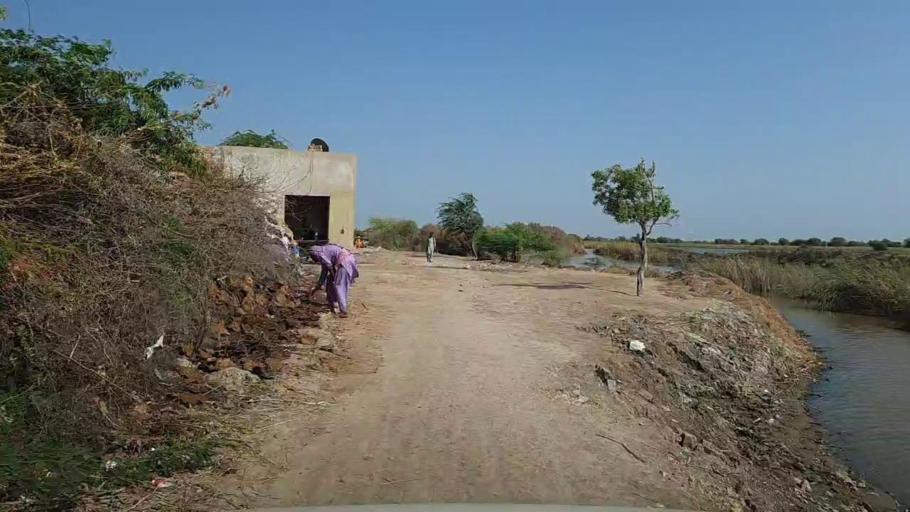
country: PK
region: Sindh
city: Kario
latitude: 24.8149
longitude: 68.5428
